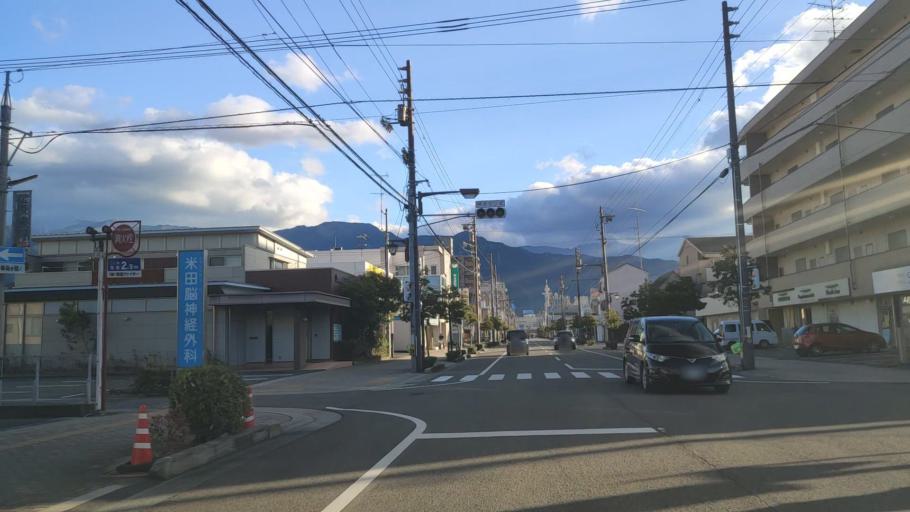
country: JP
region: Ehime
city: Saijo
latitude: 33.9166
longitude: 133.1861
